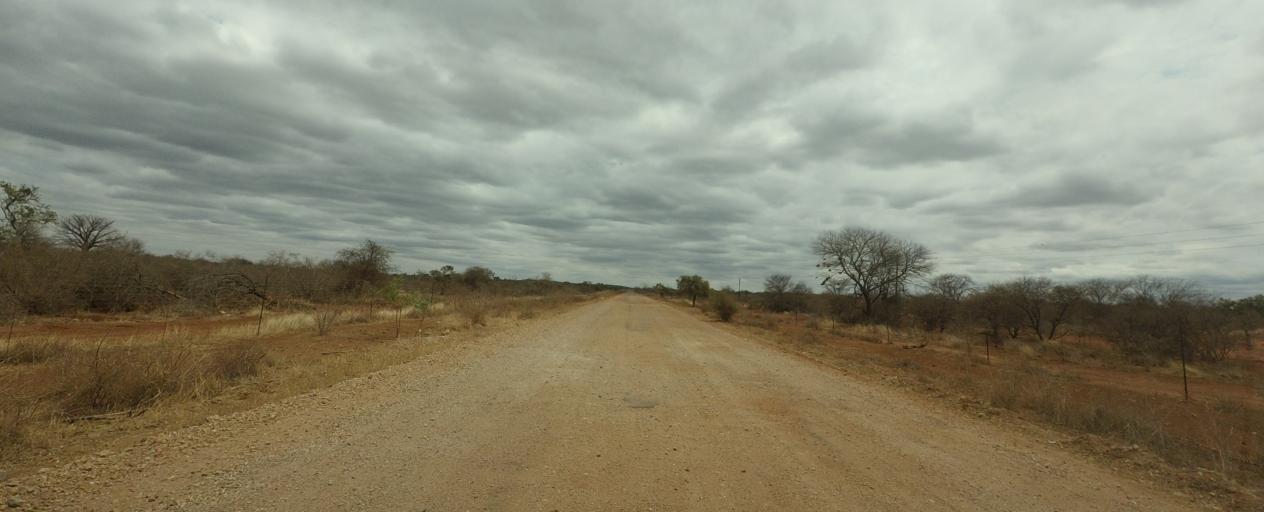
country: BW
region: Central
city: Mathathane
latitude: -22.7396
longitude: 28.4769
